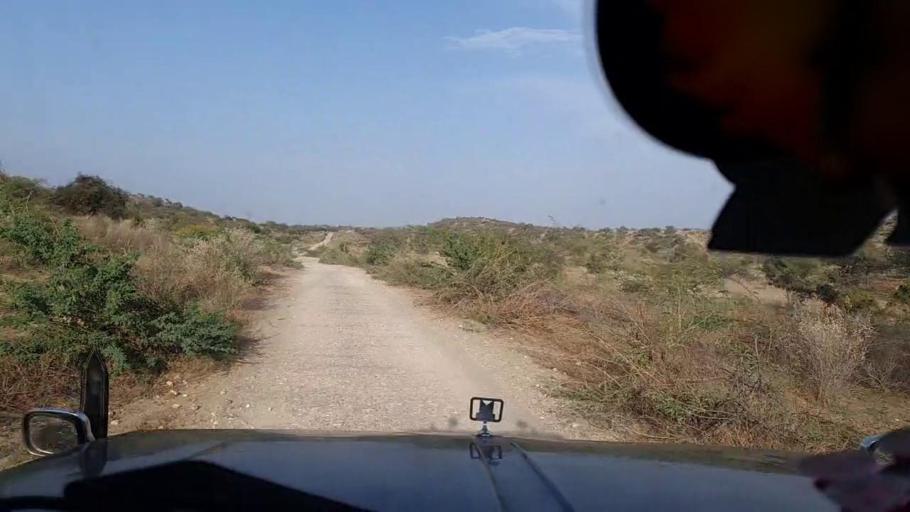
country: PK
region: Sindh
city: Diplo
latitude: 24.5543
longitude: 69.4666
